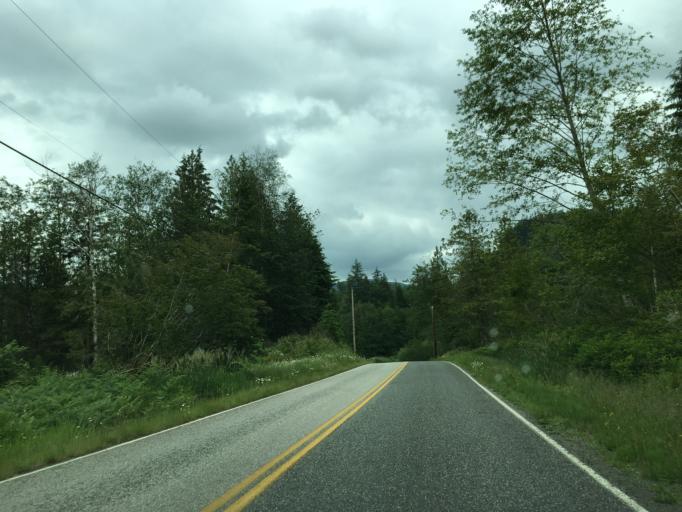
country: US
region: Washington
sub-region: Whatcom County
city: Peaceful Valley
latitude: 48.9930
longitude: -122.0697
